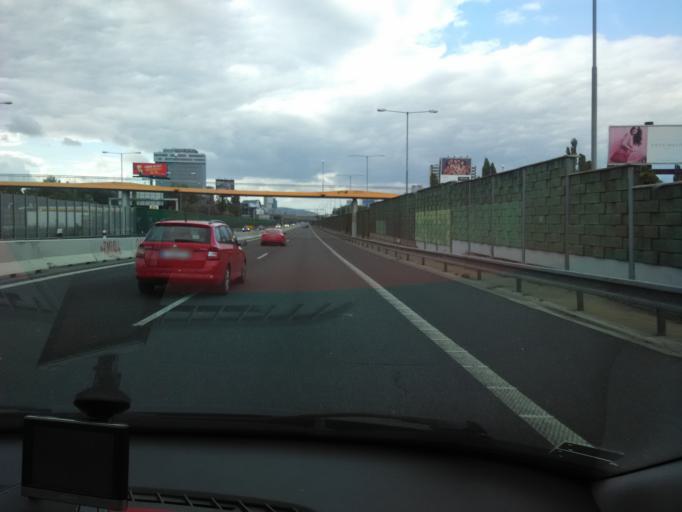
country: SK
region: Bratislavsky
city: Bratislava
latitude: 48.1311
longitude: 17.1242
